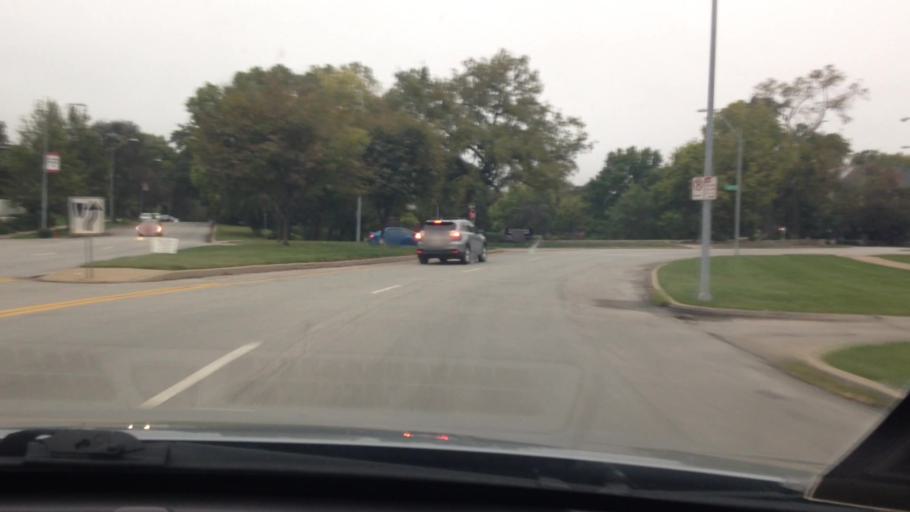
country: US
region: Missouri
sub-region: Jackson County
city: Kansas City
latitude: 39.0624
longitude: -94.5812
